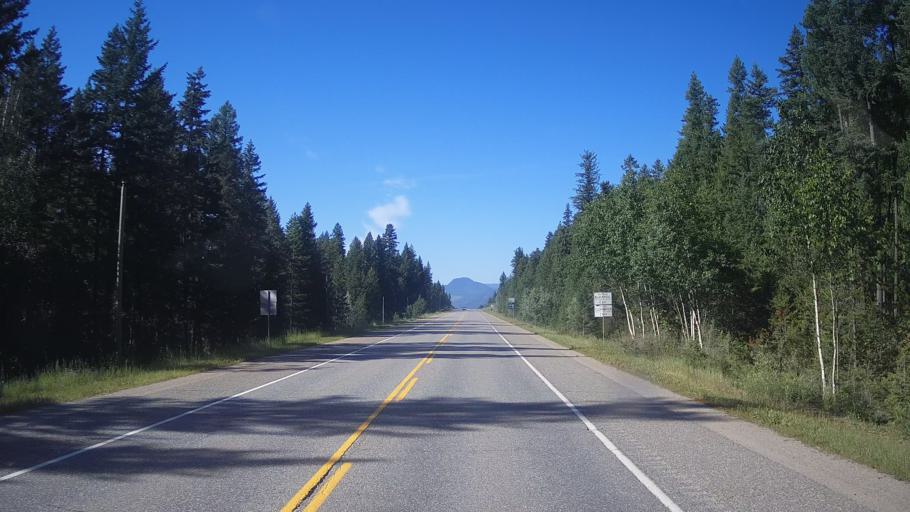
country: CA
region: British Columbia
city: Chase
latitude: 51.6321
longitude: -120.0907
